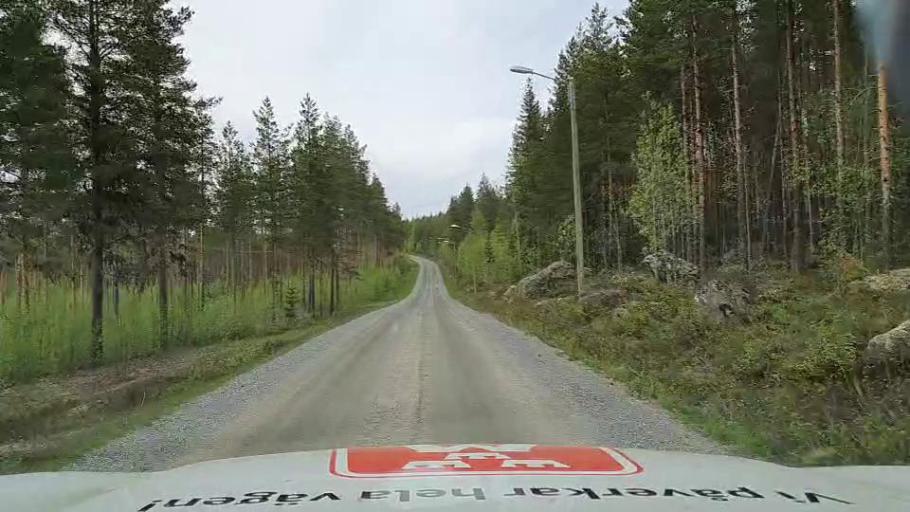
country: SE
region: Jaemtland
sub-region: Braecke Kommun
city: Braecke
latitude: 62.4597
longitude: 14.9178
